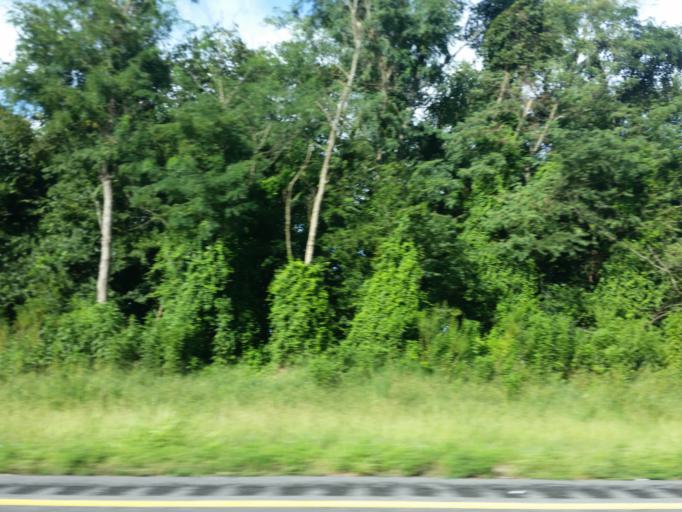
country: US
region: Tennessee
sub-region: Montgomery County
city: Clarksville
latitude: 36.5751
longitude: -87.2612
